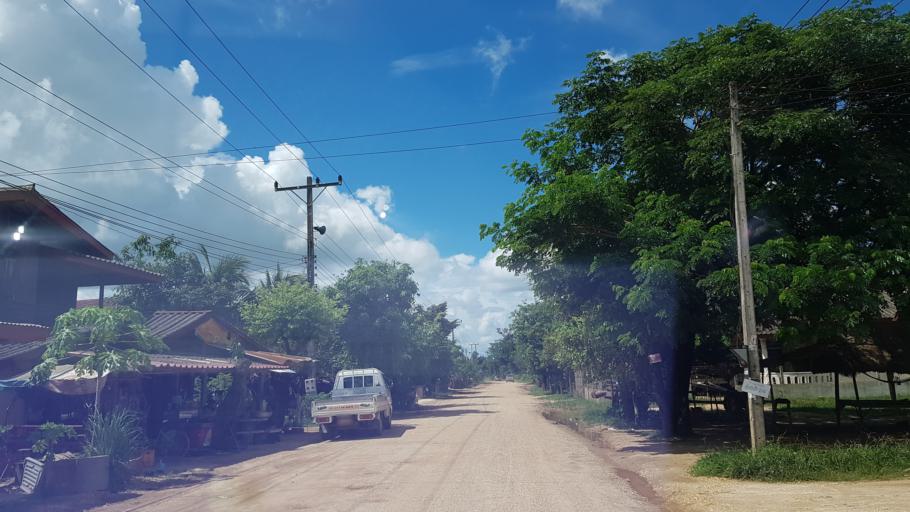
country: LA
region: Vientiane
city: Vientiane
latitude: 18.2158
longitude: 102.5154
